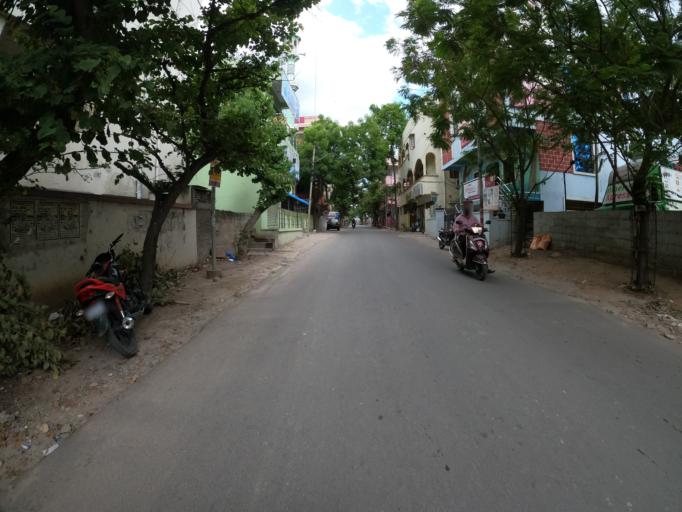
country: IN
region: Telangana
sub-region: Hyderabad
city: Hyderabad
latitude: 17.4071
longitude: 78.3901
